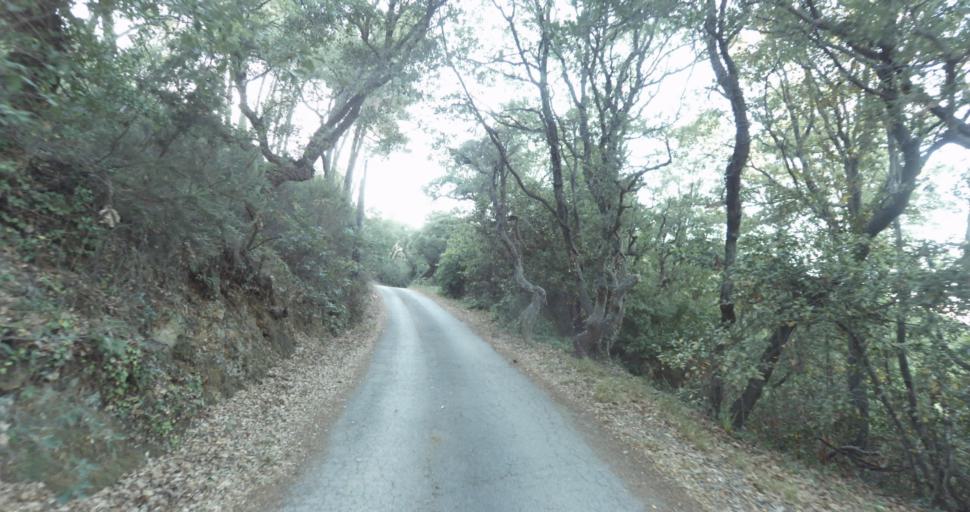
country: FR
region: Provence-Alpes-Cote d'Azur
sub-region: Departement du Var
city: Gassin
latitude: 43.2244
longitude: 6.5905
